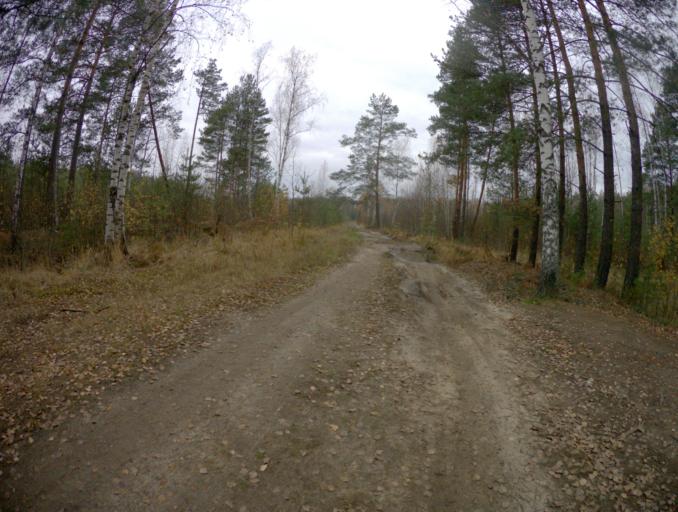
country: RU
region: Moskovskaya
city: Malaya Dubna
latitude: 55.9415
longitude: 38.9827
